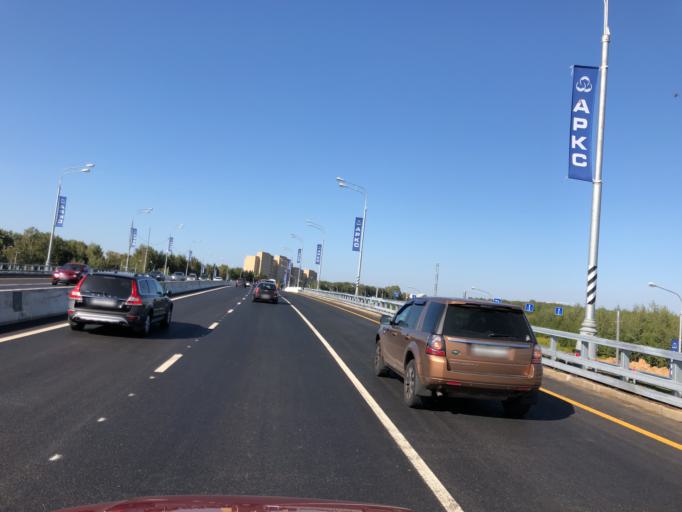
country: RU
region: Moskovskaya
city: Vatutinki
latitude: 55.4976
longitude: 37.3330
